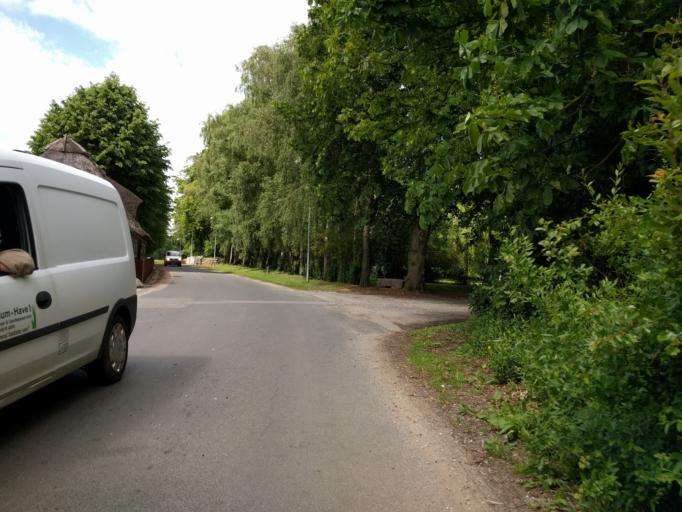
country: DK
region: South Denmark
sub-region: Odense Kommune
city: Bullerup
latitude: 55.4271
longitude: 10.4931
